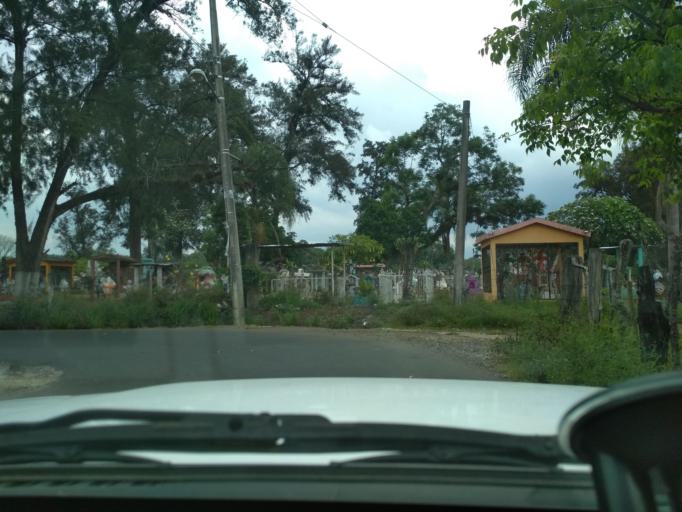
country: MX
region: Veracruz
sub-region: Cordoba
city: San Jose de Abajo [Unidad Habitacional]
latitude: 18.9235
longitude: -96.9610
